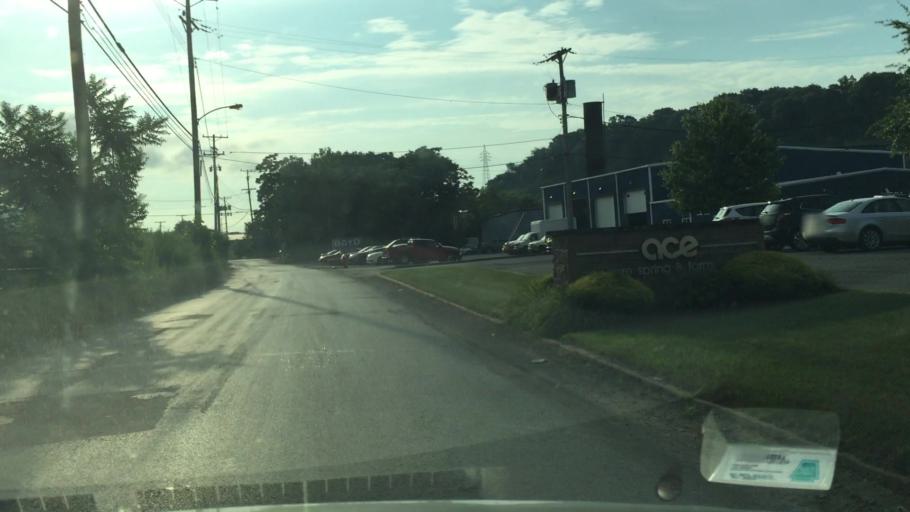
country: US
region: Pennsylvania
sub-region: Allegheny County
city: McKees Rocks
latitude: 40.4632
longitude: -80.0699
